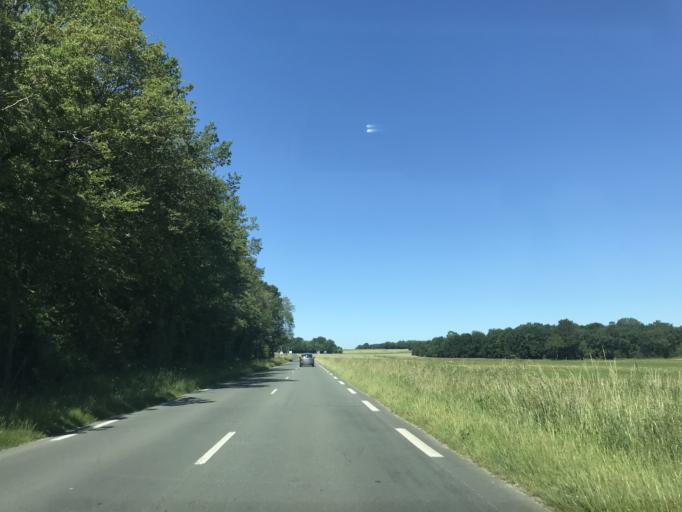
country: FR
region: Poitou-Charentes
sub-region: Departement de la Charente-Maritime
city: Cozes
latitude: 45.5790
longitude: -0.7895
